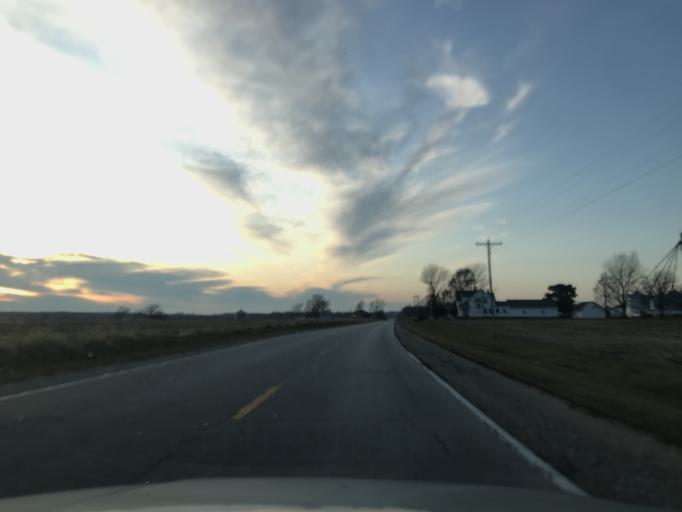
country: US
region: Illinois
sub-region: Henderson County
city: Oquawka
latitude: 41.0184
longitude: -90.7969
